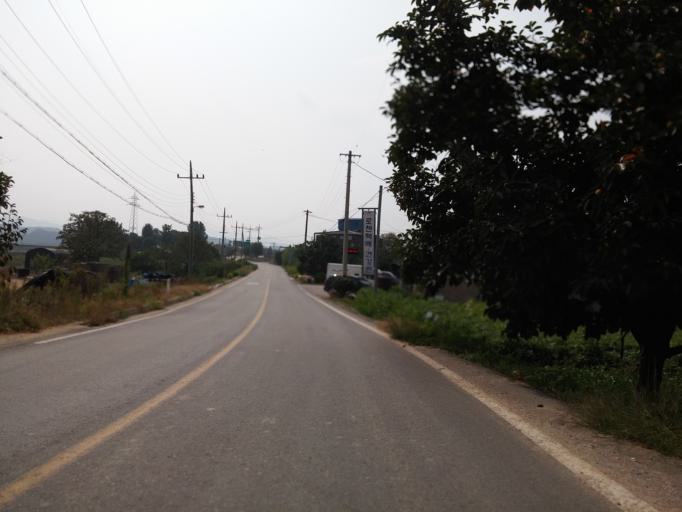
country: KR
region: Chungcheongbuk-do
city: Yong-dong
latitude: 36.3446
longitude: 127.8003
